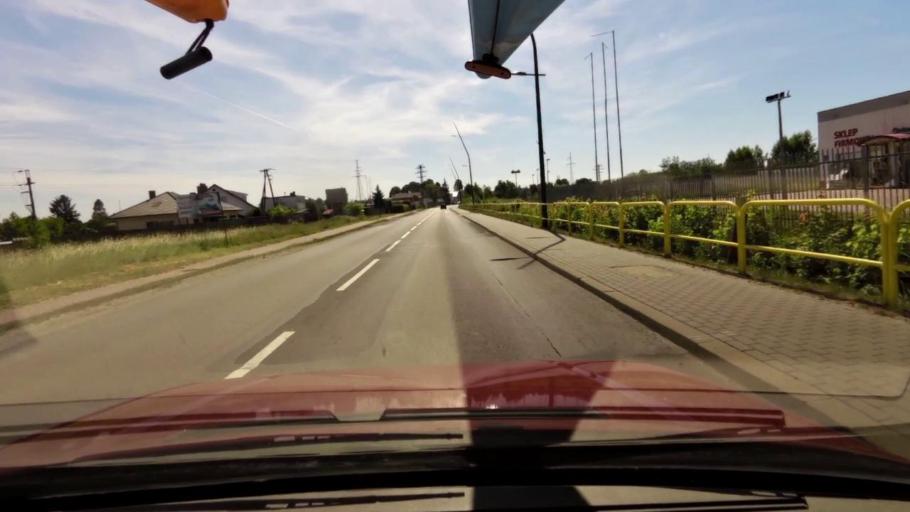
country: PL
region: Pomeranian Voivodeship
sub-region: Powiat slupski
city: Kobylnica
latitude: 54.4475
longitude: 17.0091
